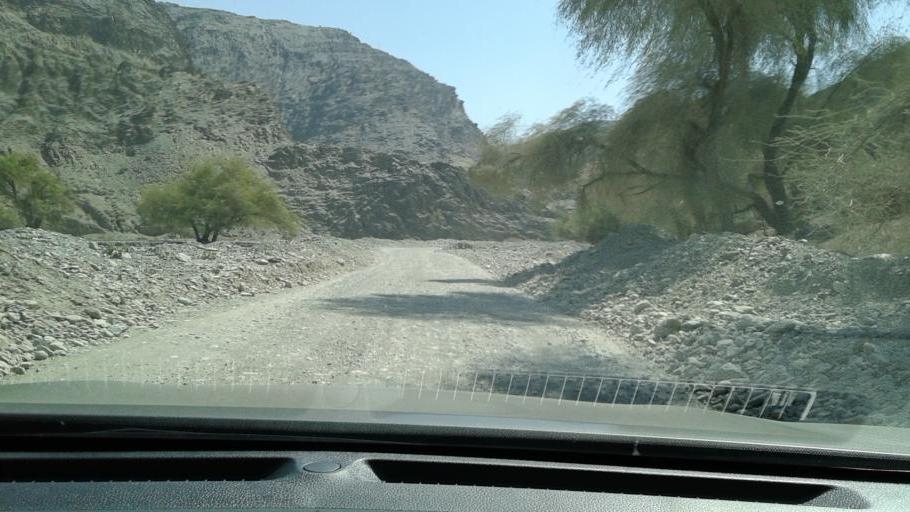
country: OM
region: Al Batinah
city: Bayt al `Awabi
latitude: 23.2602
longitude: 57.4421
